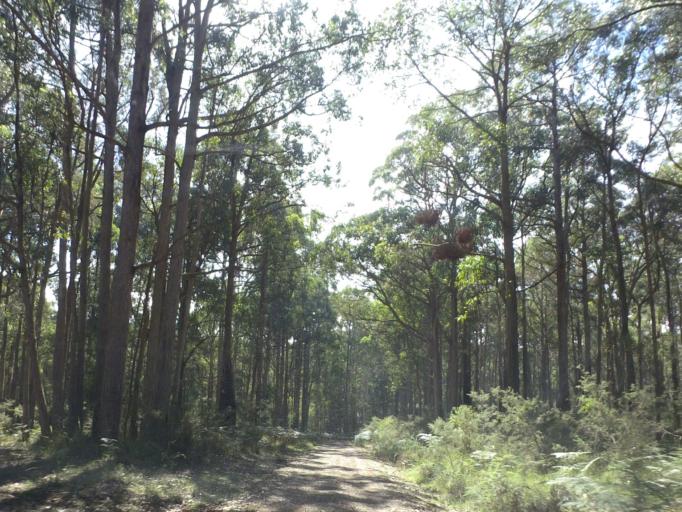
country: AU
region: Victoria
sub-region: Moorabool
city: Bacchus Marsh
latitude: -37.4352
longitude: 144.2769
